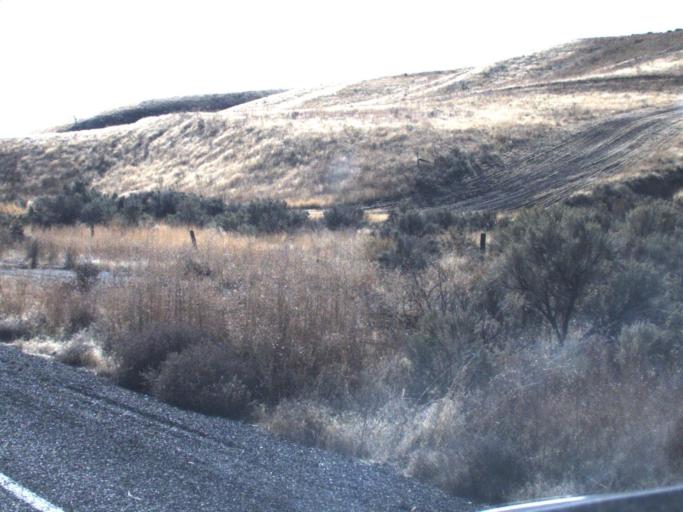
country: US
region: Washington
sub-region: Franklin County
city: Connell
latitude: 46.6609
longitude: -118.5478
